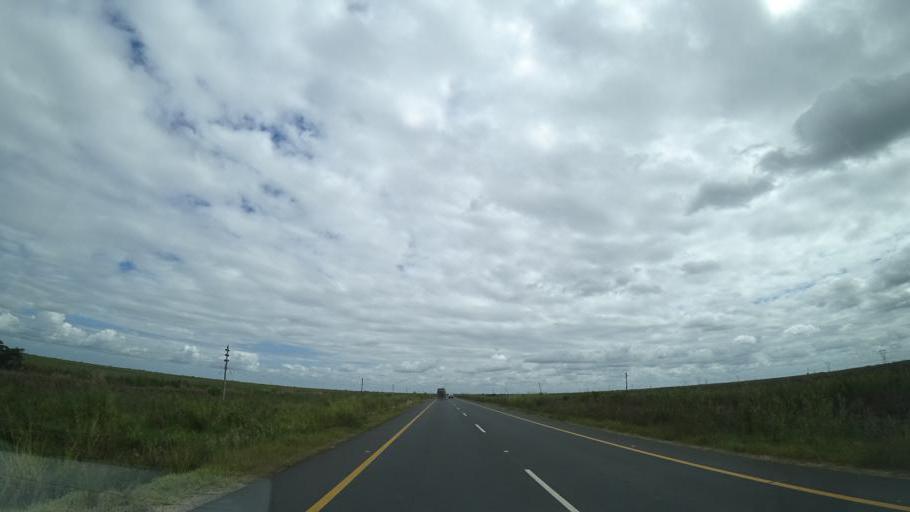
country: MZ
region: Sofala
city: Dondo
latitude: -19.4883
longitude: 34.5821
